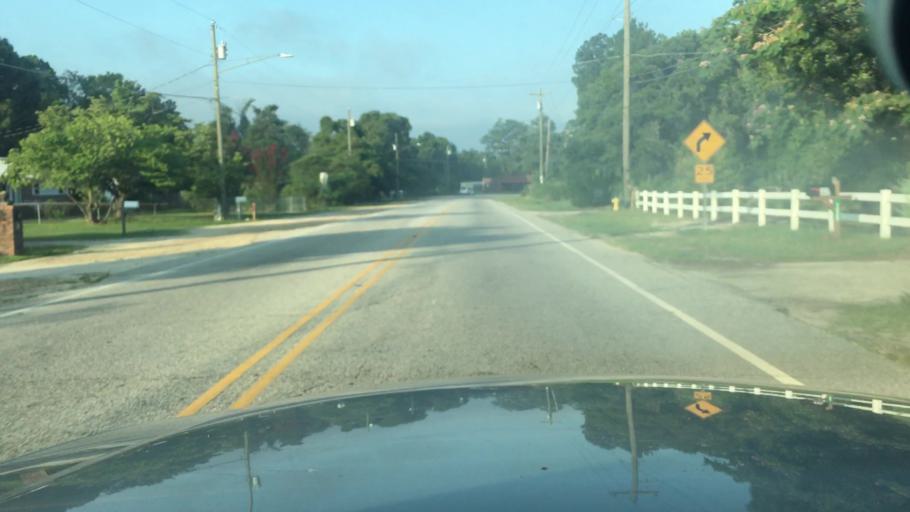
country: US
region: North Carolina
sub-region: Cumberland County
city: Spring Lake
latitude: 35.1095
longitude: -78.9359
